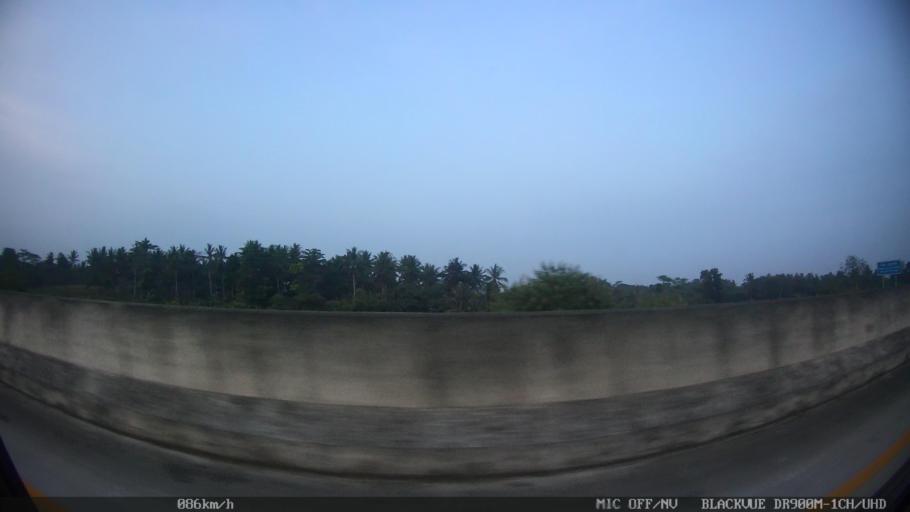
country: ID
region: Lampung
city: Kalianda
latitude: -5.6735
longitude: 105.6035
